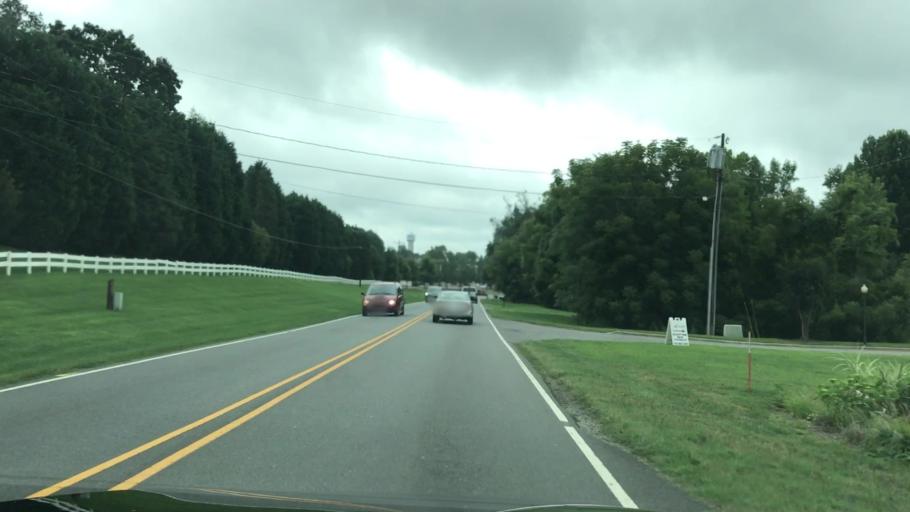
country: US
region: North Carolina
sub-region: Iredell County
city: Mooresville
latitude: 35.5707
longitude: -80.8672
